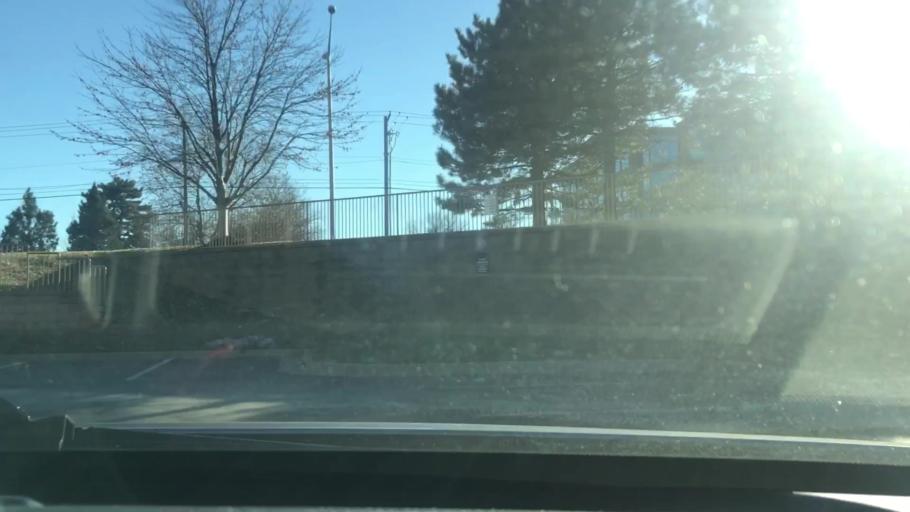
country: US
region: Kansas
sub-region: Johnson County
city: Leawood
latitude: 38.9279
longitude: -94.6533
